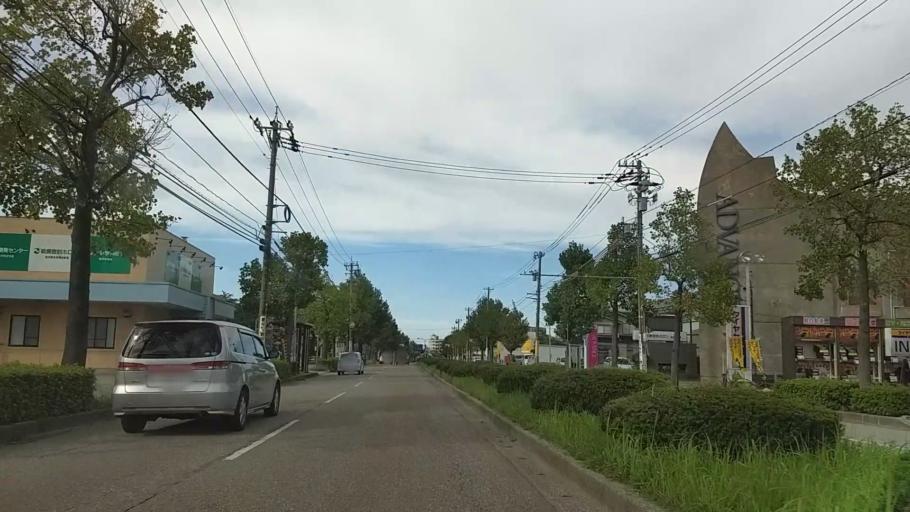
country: JP
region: Ishikawa
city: Nonoichi
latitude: 36.5367
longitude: 136.6394
